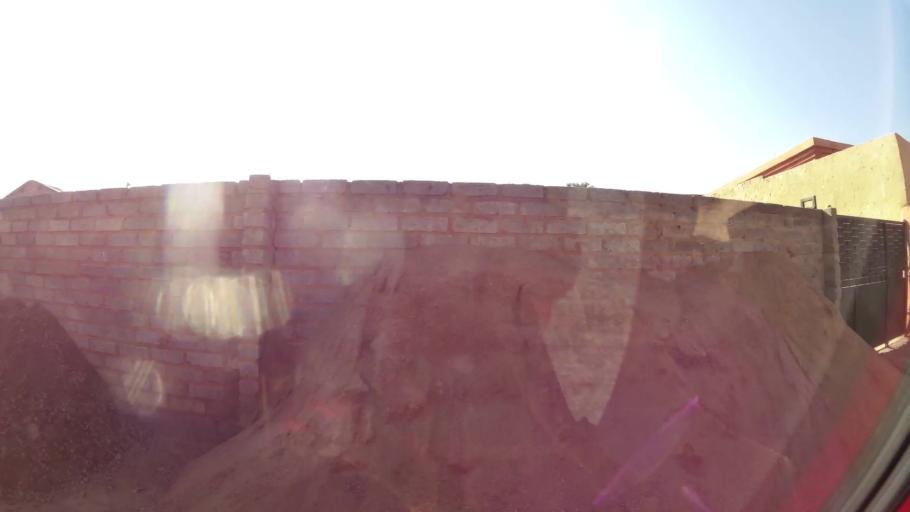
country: ZA
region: Gauteng
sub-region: City of Johannesburg Metropolitan Municipality
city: Soweto
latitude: -26.2460
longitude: 27.9508
